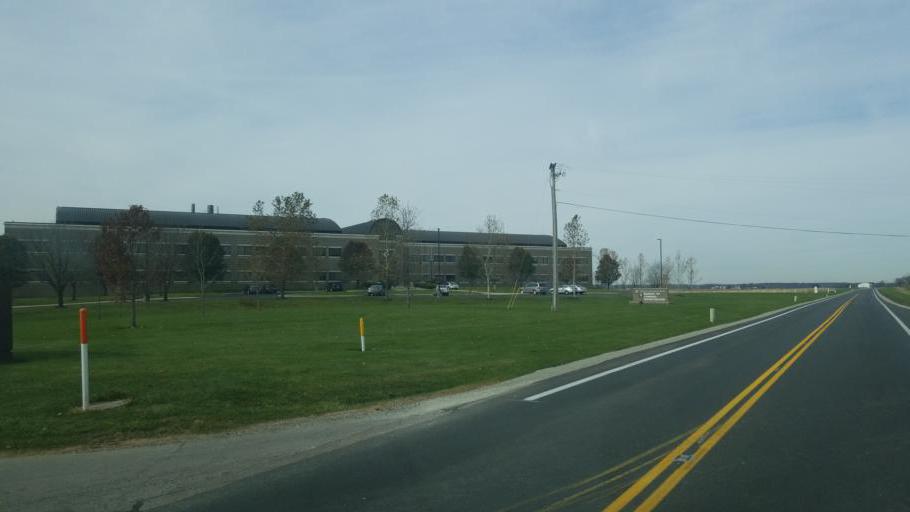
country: US
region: Ohio
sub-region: Madison County
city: London
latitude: 39.9118
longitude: -83.4758
